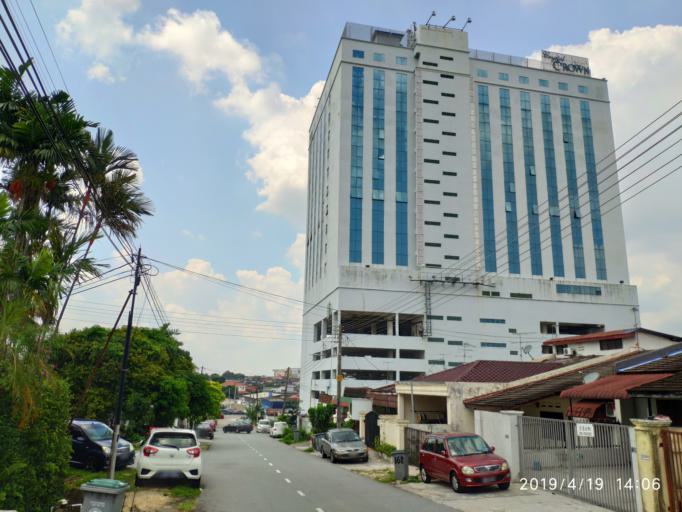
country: MY
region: Johor
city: Johor Bahru
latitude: 1.4862
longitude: 103.7653
